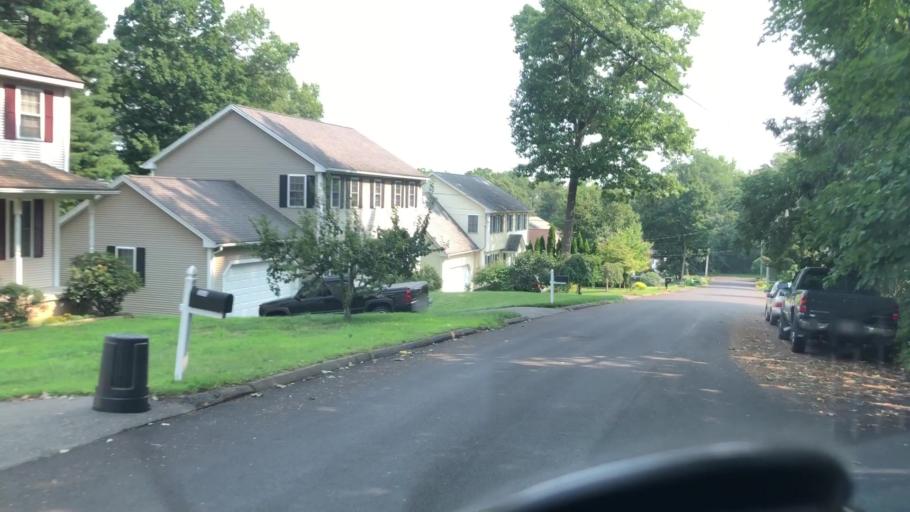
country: US
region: Massachusetts
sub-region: Hampden County
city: Holyoke
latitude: 42.1734
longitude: -72.6502
